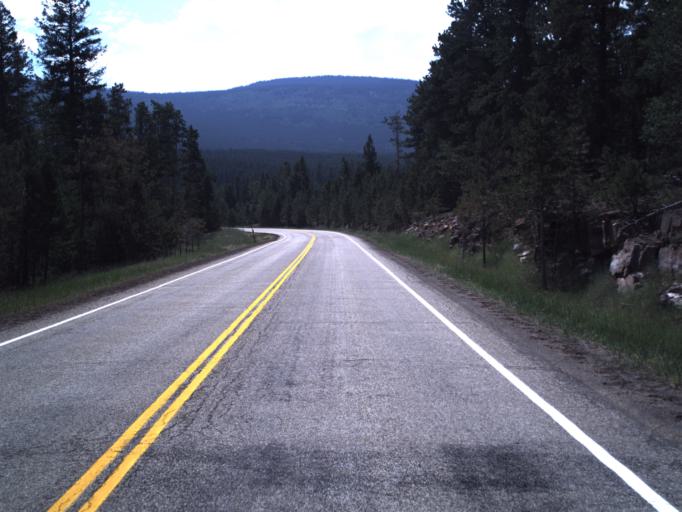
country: US
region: Utah
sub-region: Daggett County
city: Manila
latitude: 40.8445
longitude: -109.6649
